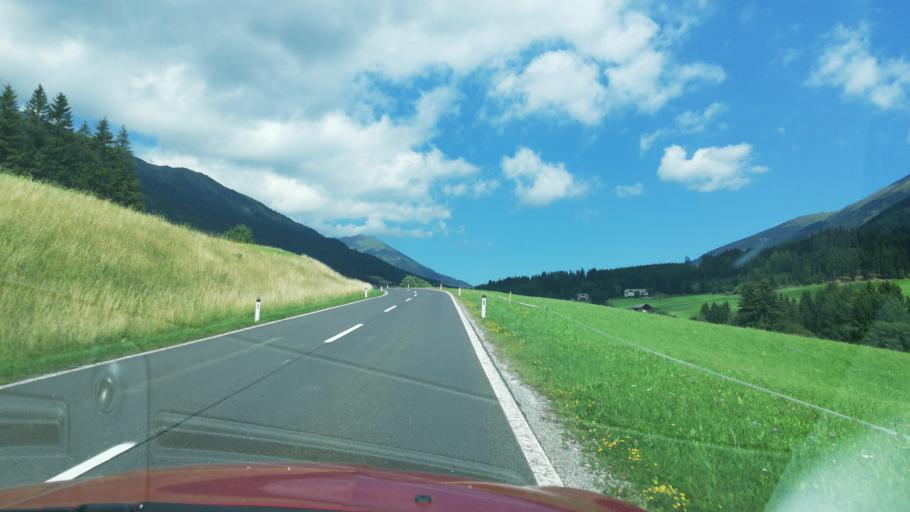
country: AT
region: Styria
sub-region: Politischer Bezirk Murtal
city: Sankt Johann am Tauern
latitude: 47.3632
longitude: 14.4665
